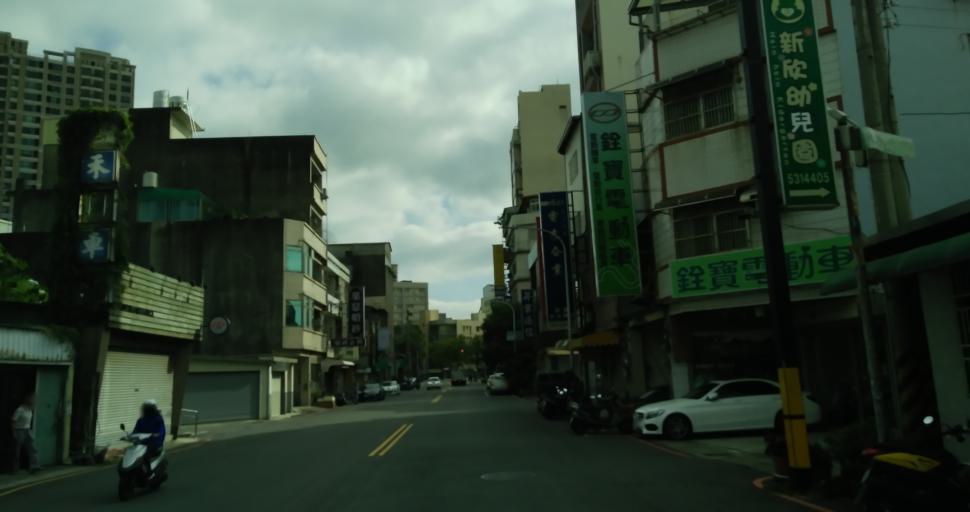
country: TW
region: Taiwan
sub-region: Hsinchu
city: Hsinchu
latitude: 24.8156
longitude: 120.9724
